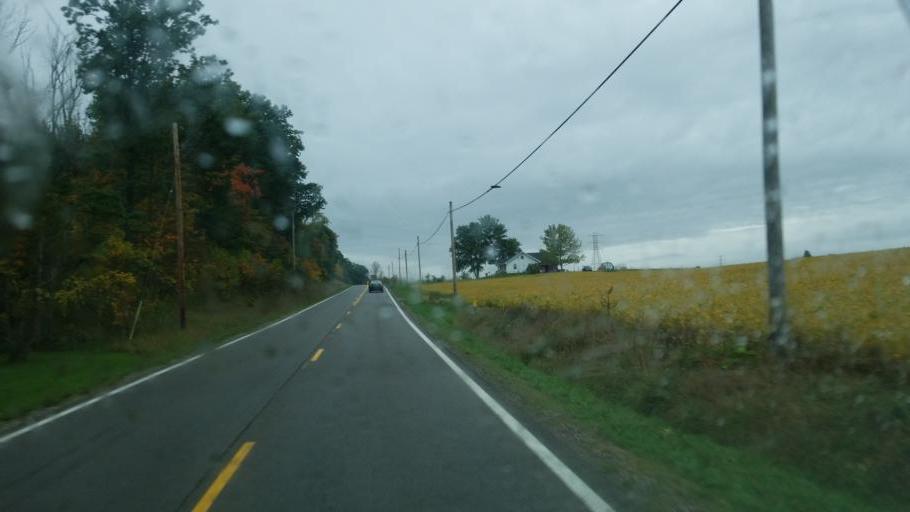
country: US
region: Ohio
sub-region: Richland County
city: Lincoln Heights
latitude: 40.8549
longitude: -82.4512
